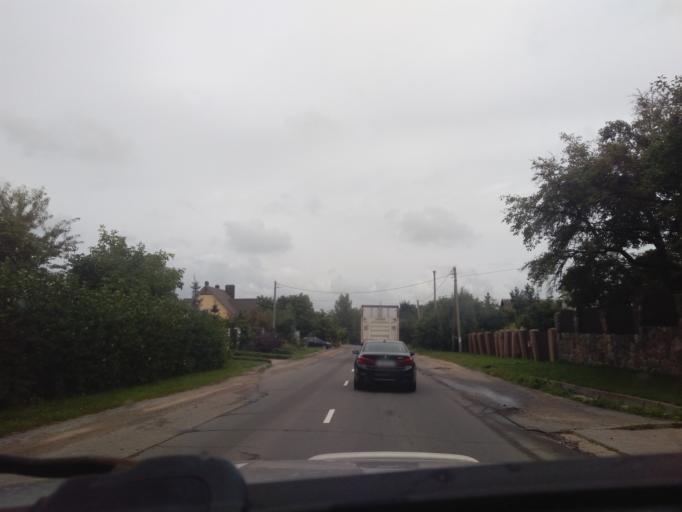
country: BY
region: Minsk
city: Zhdanovichy
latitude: 53.9190
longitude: 27.3900
